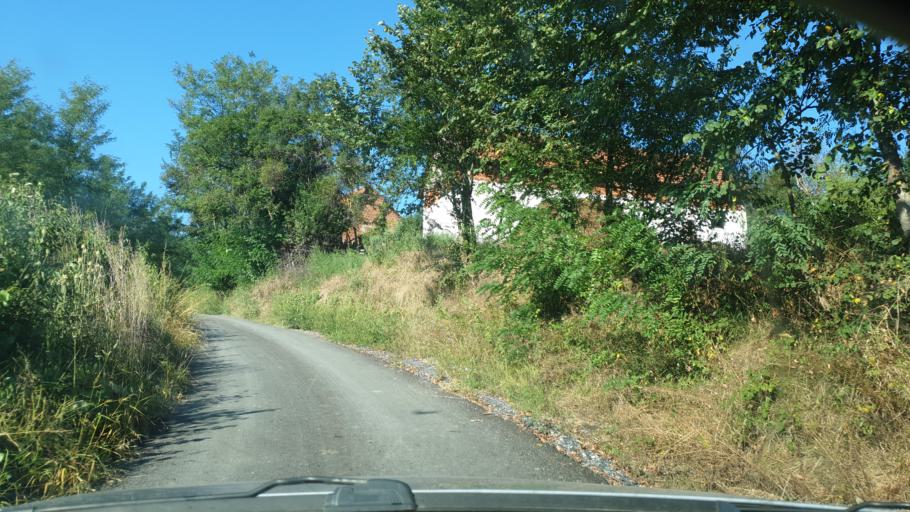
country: RS
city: Jarebice
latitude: 44.5036
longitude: 19.4838
